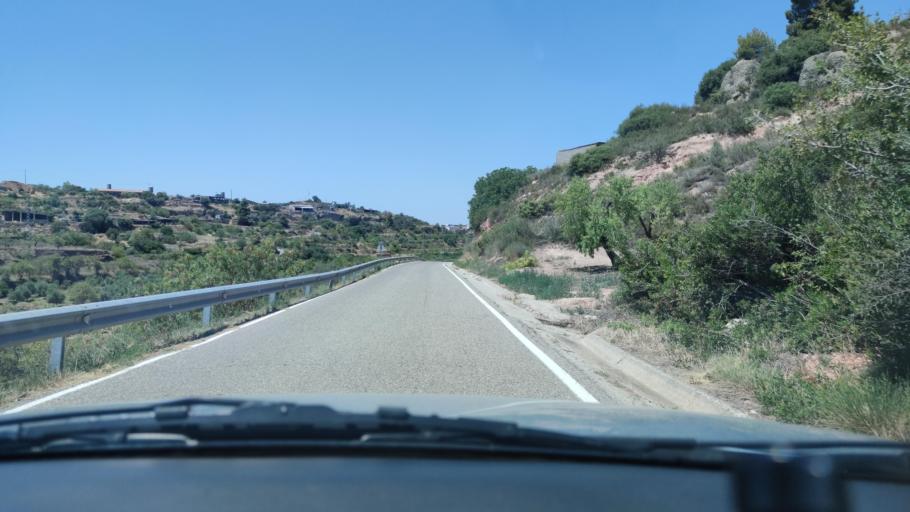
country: ES
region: Catalonia
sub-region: Provincia de Lleida
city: Juncosa
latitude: 41.3671
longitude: 0.7785
